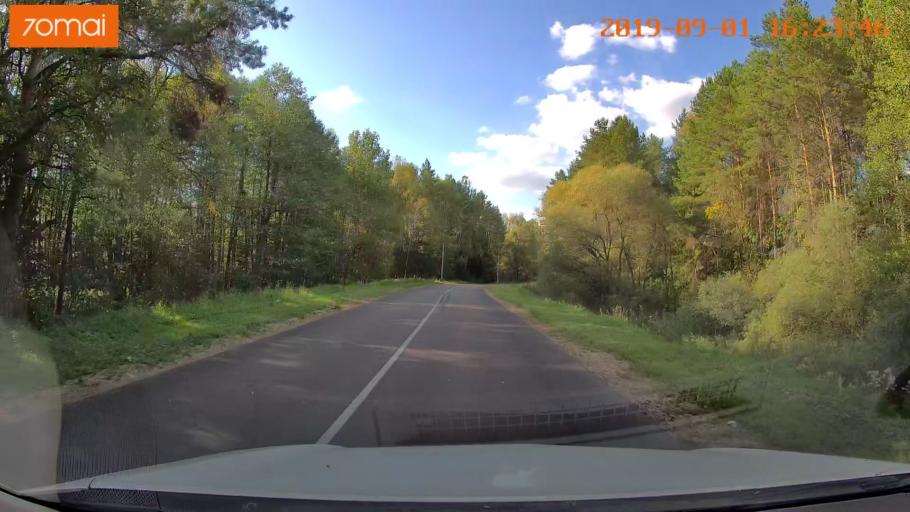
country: RU
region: Kaluga
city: Maloyaroslavets
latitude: 54.8842
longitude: 36.5304
